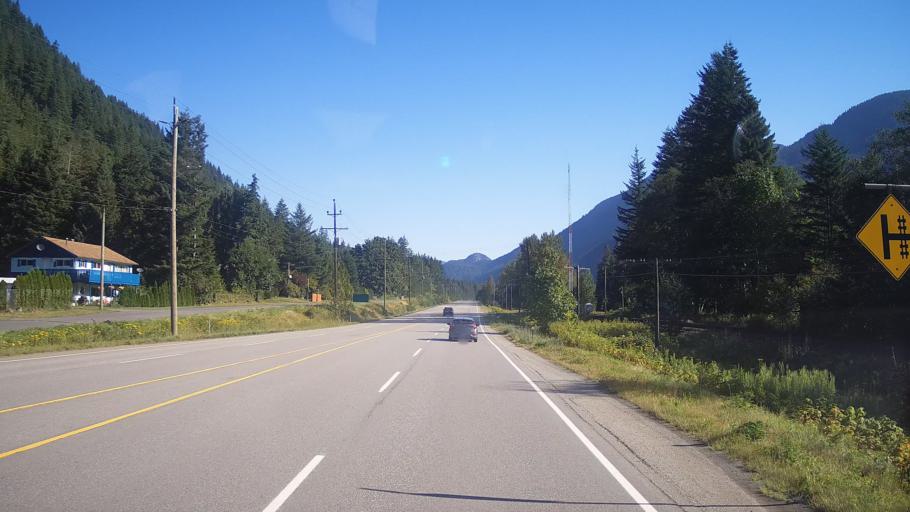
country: CA
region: British Columbia
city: Hope
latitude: 49.4898
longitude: -121.4209
